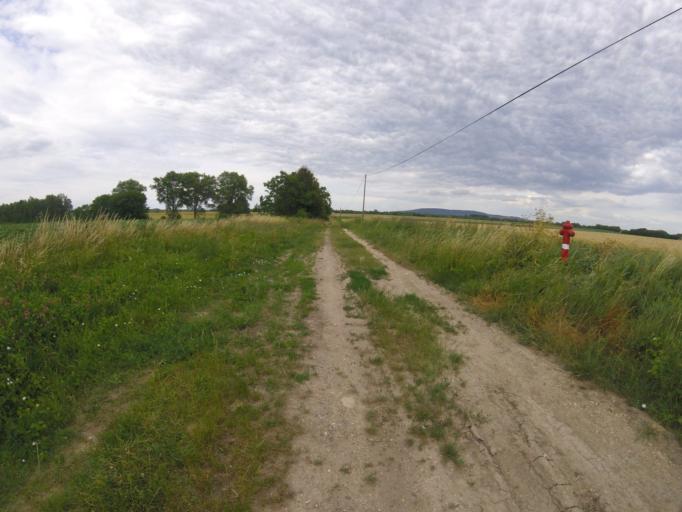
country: HU
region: Zala
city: Turje
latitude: 46.9907
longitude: 17.1862
